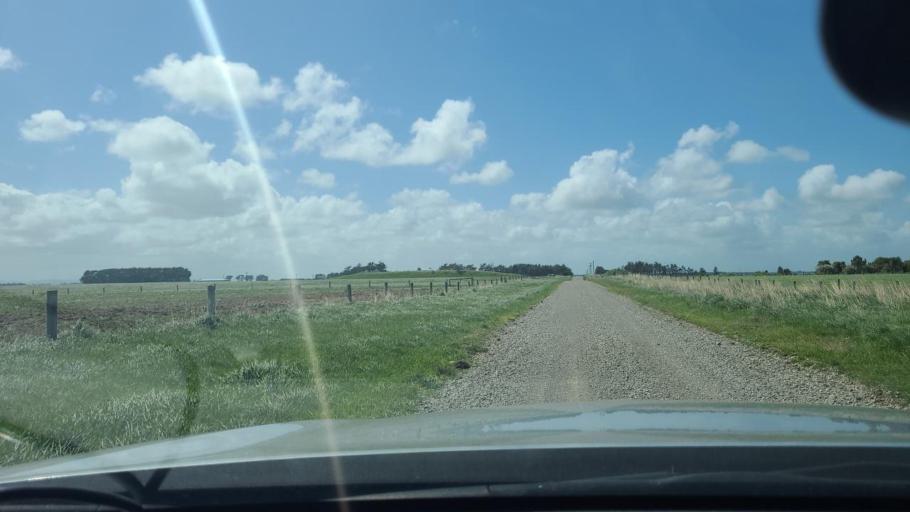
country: NZ
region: Southland
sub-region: Invercargill City
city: Invercargill
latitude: -46.3457
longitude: 168.1881
